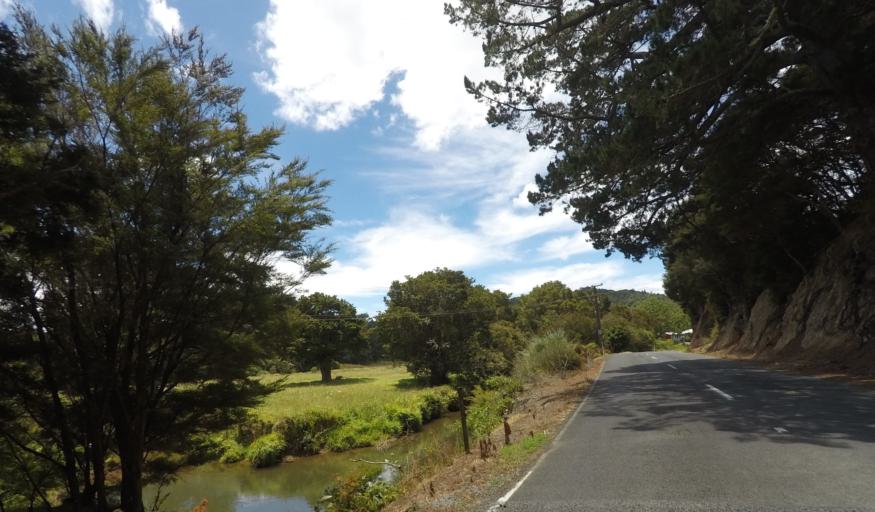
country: NZ
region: Northland
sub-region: Whangarei
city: Ngunguru
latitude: -35.5048
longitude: 174.4275
